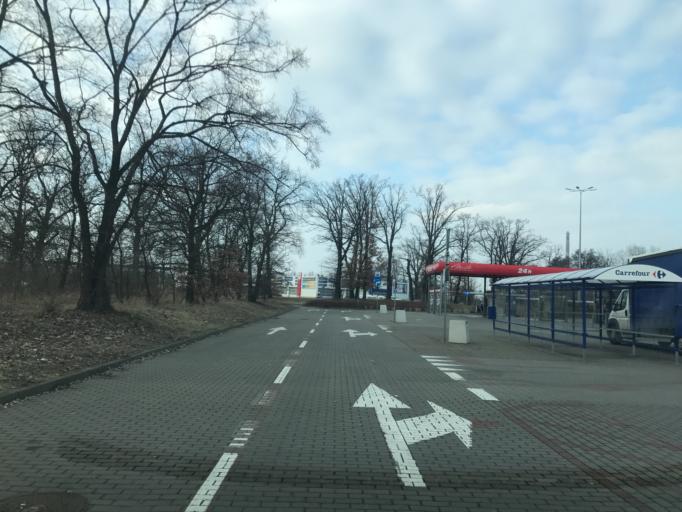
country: PL
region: Kujawsko-Pomorskie
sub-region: Powiat torunski
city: Lubicz Dolny
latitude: 53.0318
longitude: 18.6915
